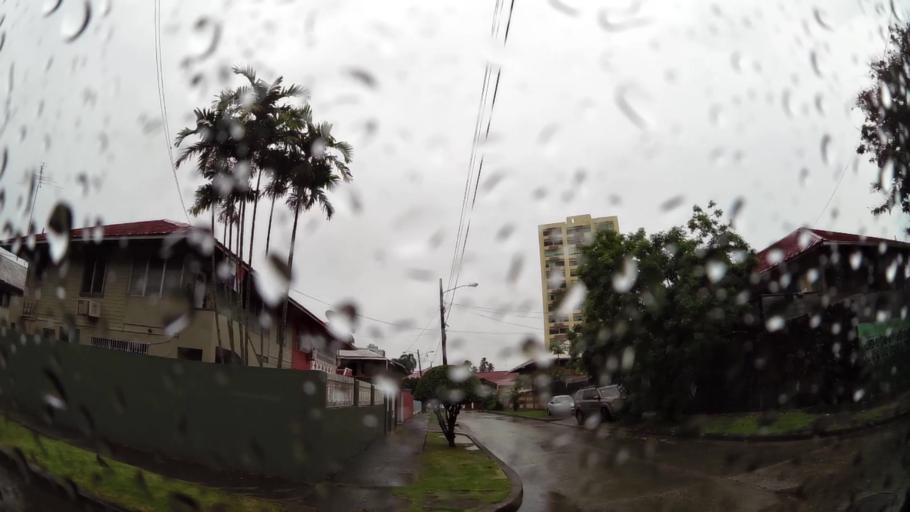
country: PA
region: Colon
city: Colon
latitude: 9.3621
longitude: -79.8981
